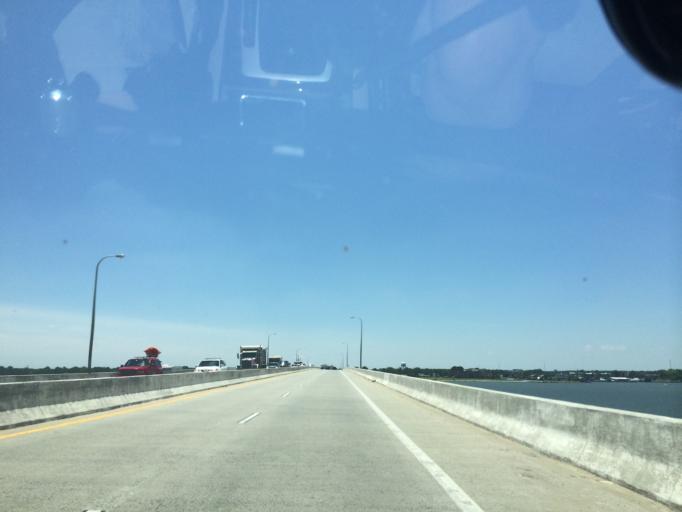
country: US
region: Maryland
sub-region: Dorchester County
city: Cambridge
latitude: 38.5812
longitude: -76.0559
